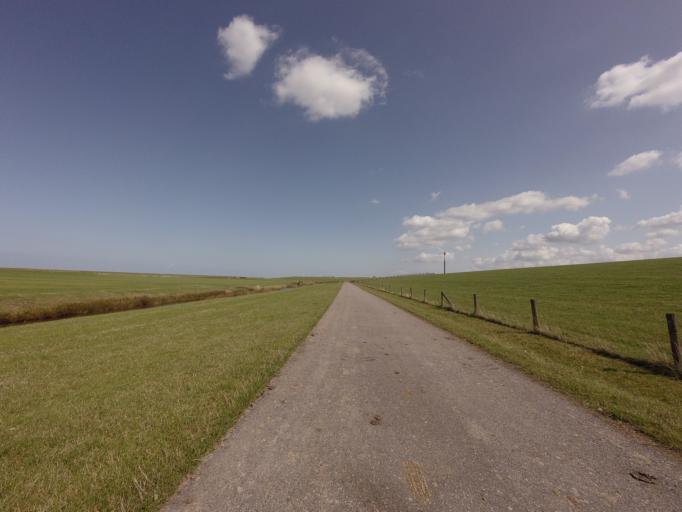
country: NL
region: Friesland
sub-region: Gemeente Ferwerderadiel
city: Marrum
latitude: 53.3328
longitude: 5.7773
